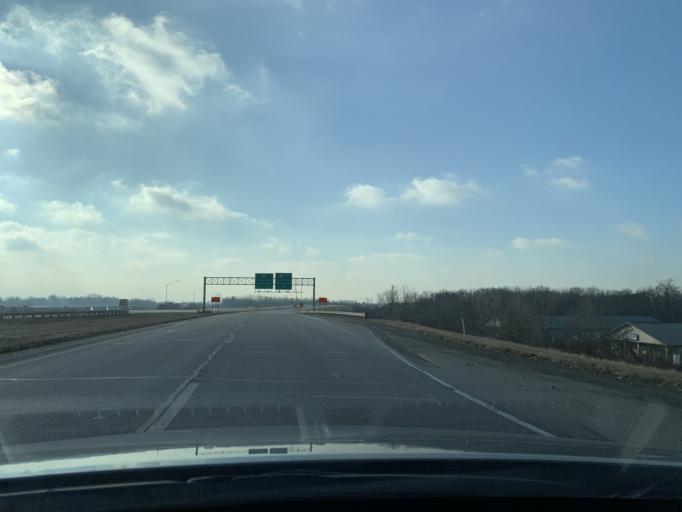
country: US
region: Indiana
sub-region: Porter County
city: Valparaiso
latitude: 41.4761
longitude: -87.0205
